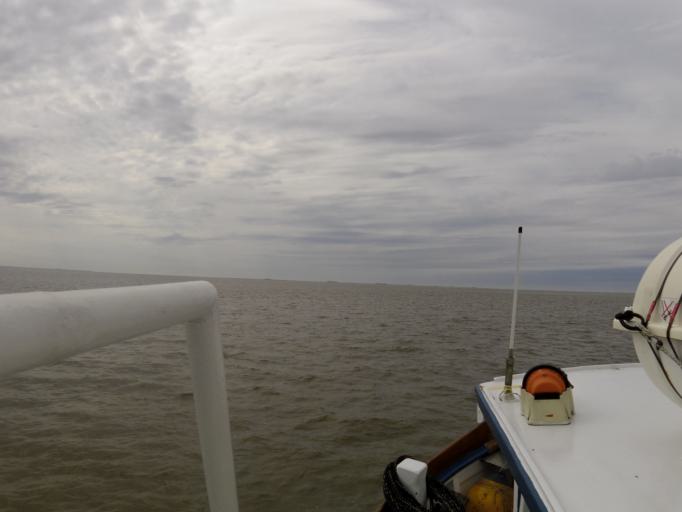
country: DE
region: Schleswig-Holstein
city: Langeness
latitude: 54.6161
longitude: 8.6368
